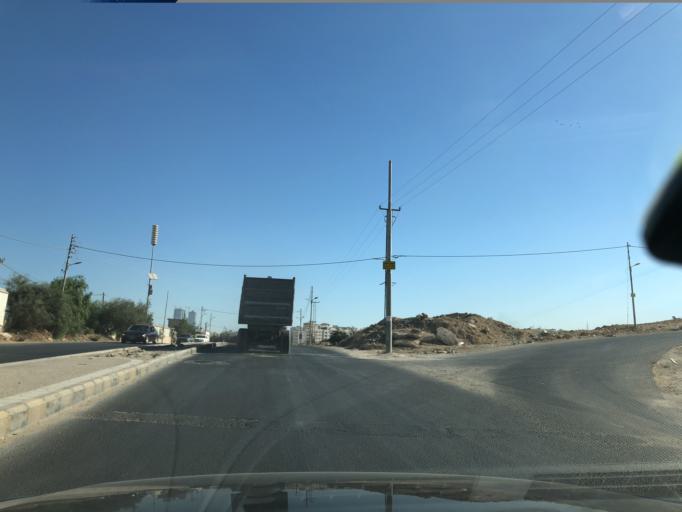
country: JO
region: Amman
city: Wadi as Sir
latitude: 31.9356
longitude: 35.8482
